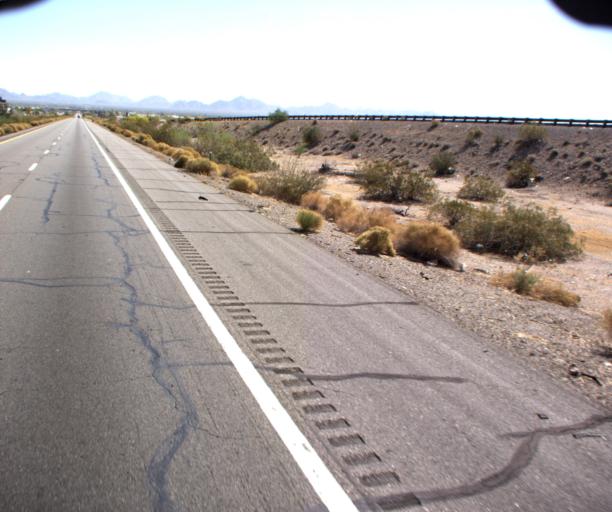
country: US
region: Arizona
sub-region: La Paz County
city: Quartzsite
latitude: 33.6596
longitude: -114.2407
